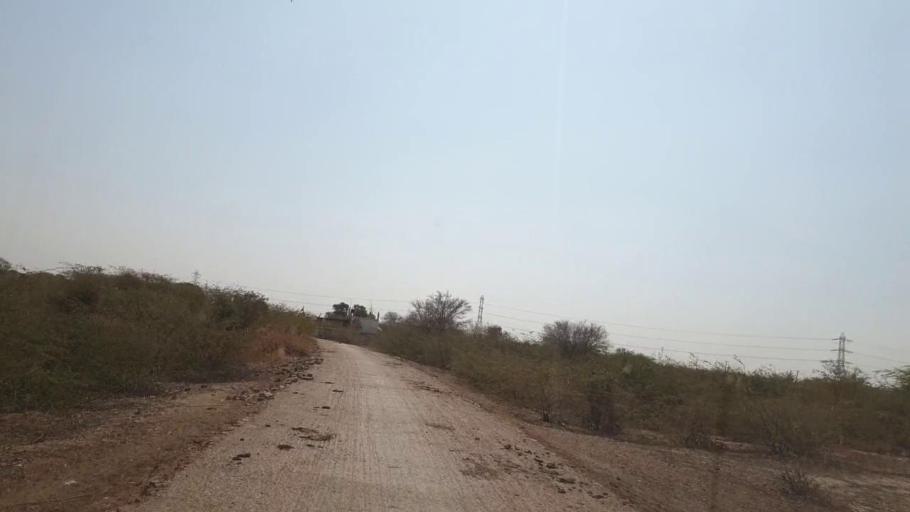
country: PK
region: Sindh
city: Nabisar
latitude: 25.0637
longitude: 69.5453
